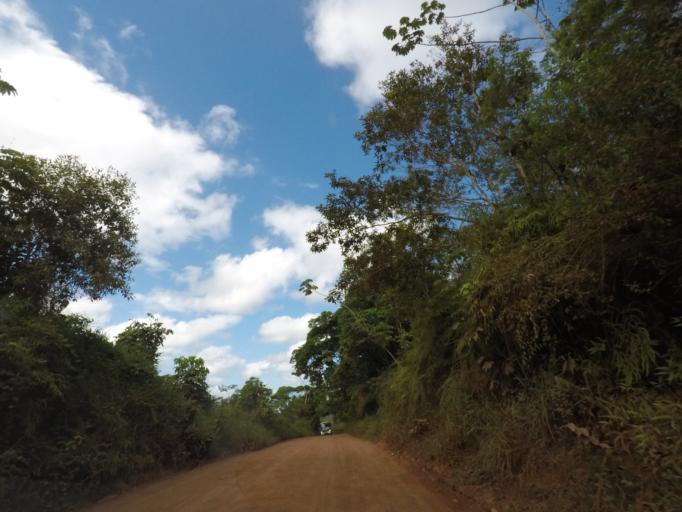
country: BR
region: Bahia
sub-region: Itacare
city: Itacare
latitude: -14.2217
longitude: -39.0930
